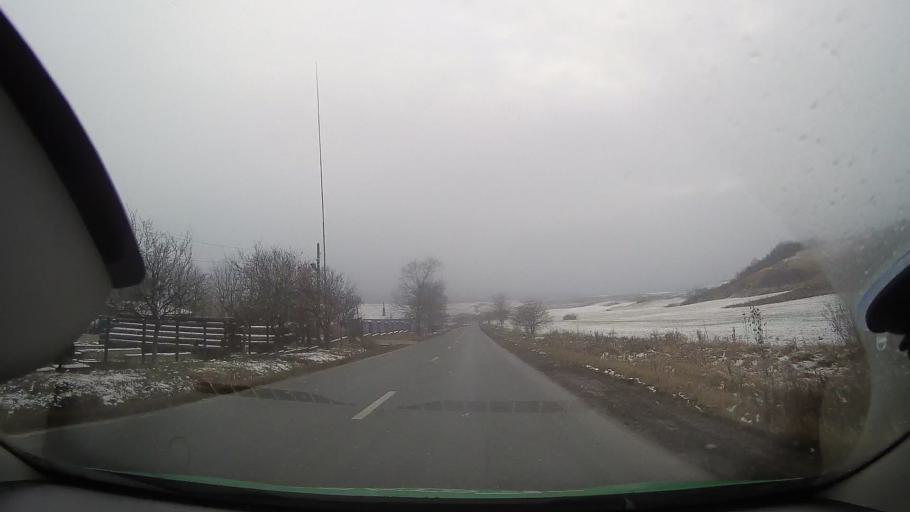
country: RO
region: Sibiu
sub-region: Comuna Blajel
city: Blajel
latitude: 46.2517
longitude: 24.2999
